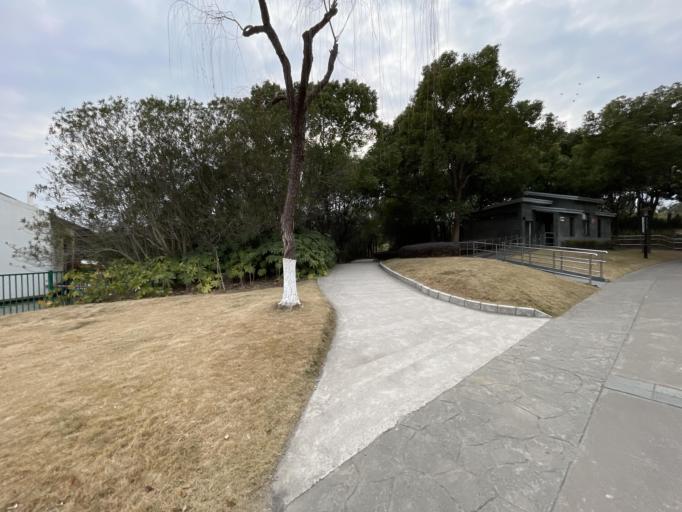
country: CN
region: Shanghai Shi
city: Yangpu
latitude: 31.2949
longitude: 121.5249
